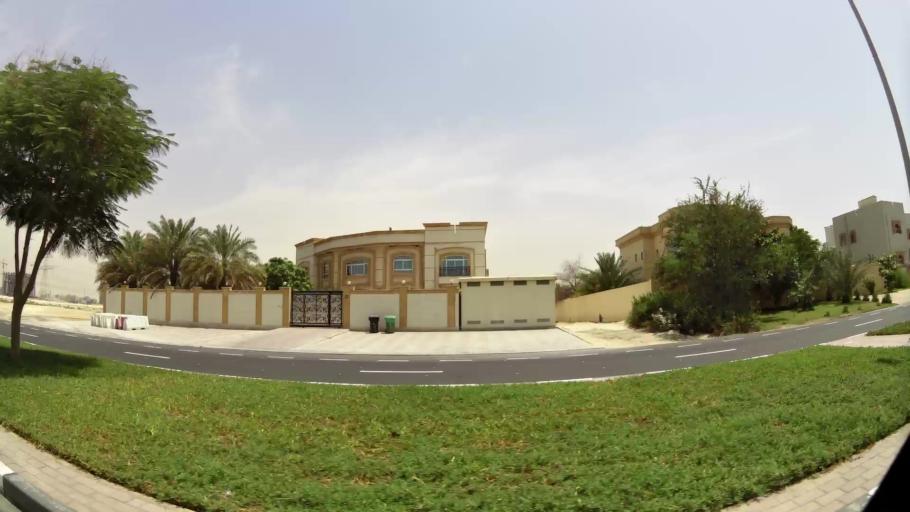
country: AE
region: Ash Shariqah
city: Sharjah
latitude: 25.2003
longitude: 55.3901
